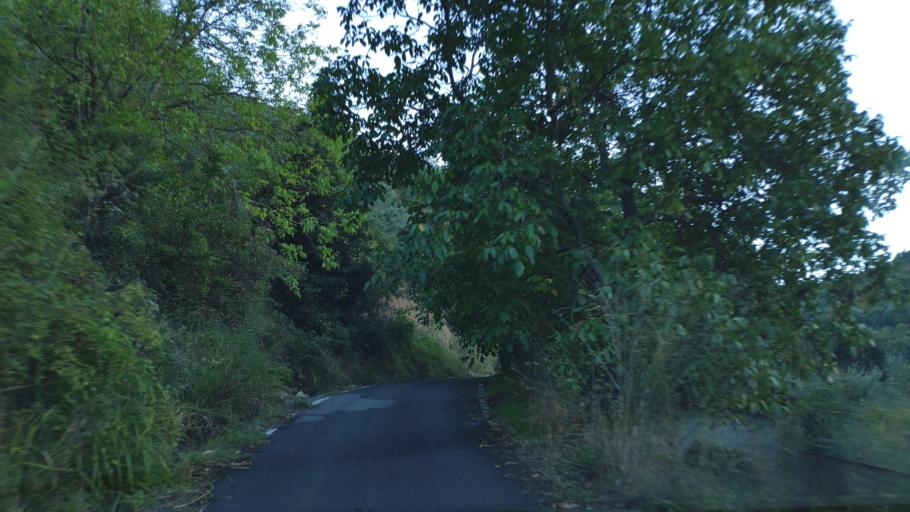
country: GR
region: Peloponnese
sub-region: Nomos Arkadias
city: Dimitsana
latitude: 37.5709
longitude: 22.0445
